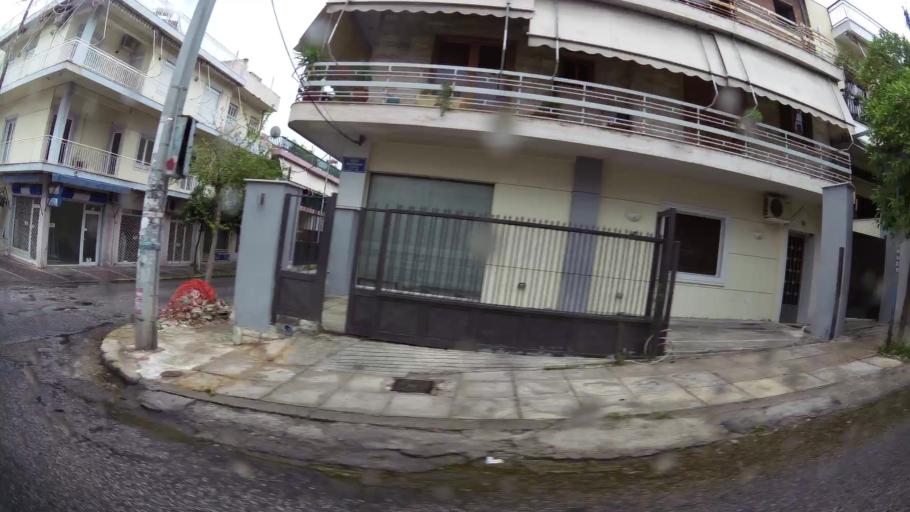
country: GR
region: Attica
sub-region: Nomos Piraios
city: Korydallos
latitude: 37.9857
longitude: 23.6410
